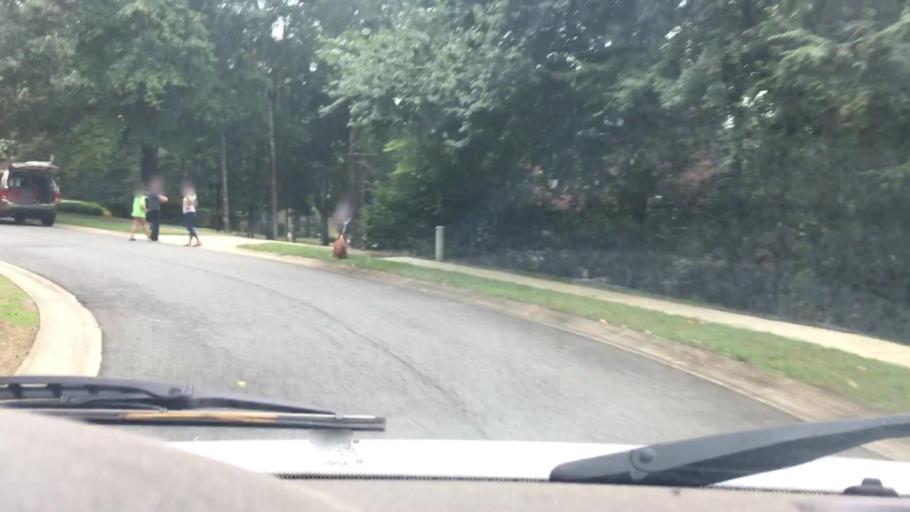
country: US
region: North Carolina
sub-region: Gaston County
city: Davidson
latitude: 35.4691
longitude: -80.7957
